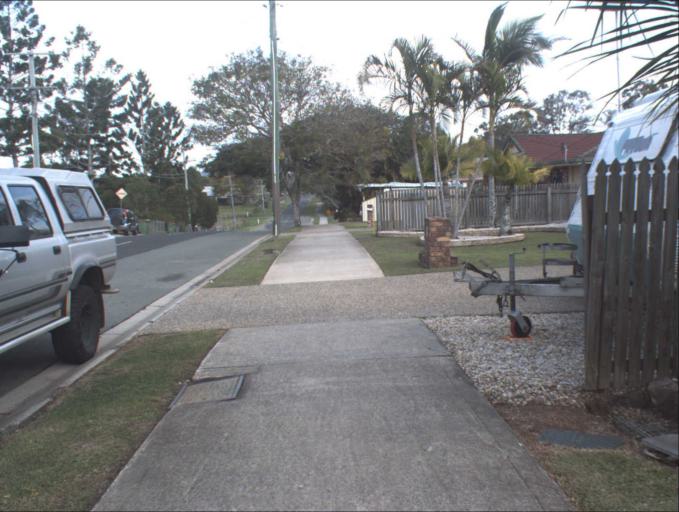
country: AU
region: Queensland
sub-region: Logan
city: Waterford West
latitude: -27.6924
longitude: 153.1281
